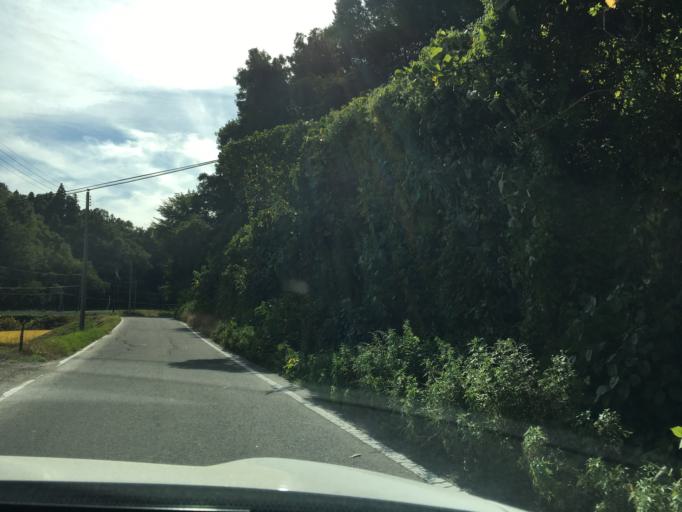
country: JP
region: Fukushima
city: Nihommatsu
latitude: 37.5243
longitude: 140.5028
